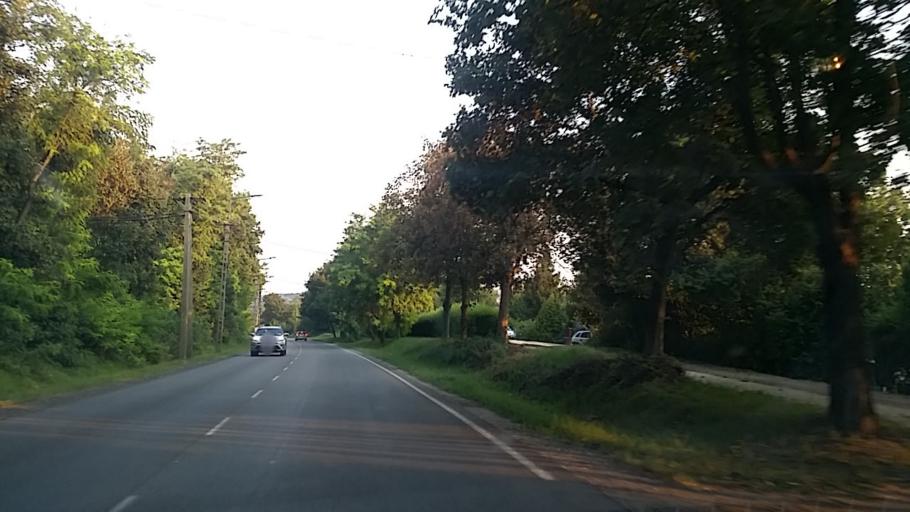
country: HU
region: Fejer
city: dunaujvaros
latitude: 46.9885
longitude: 18.9308
